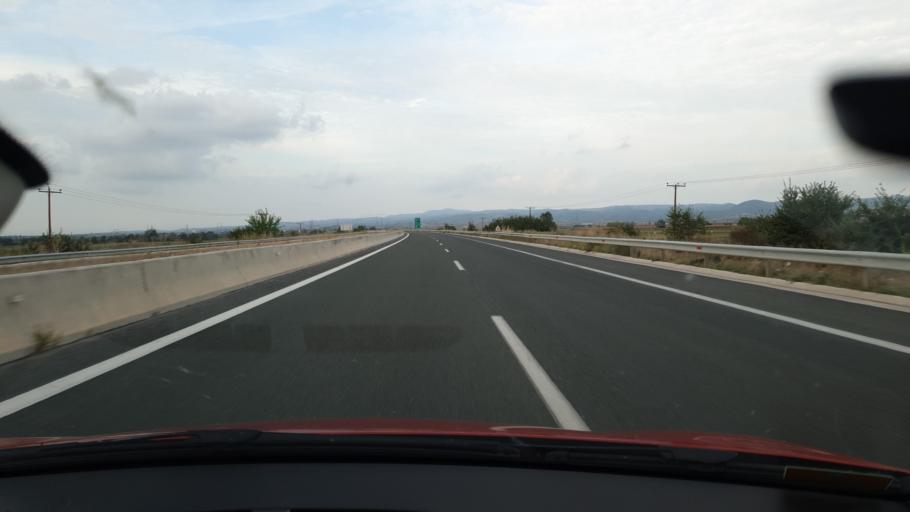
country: GR
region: Central Macedonia
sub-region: Nomos Thessalonikis
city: Lagkadas
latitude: 40.7699
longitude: 23.0221
